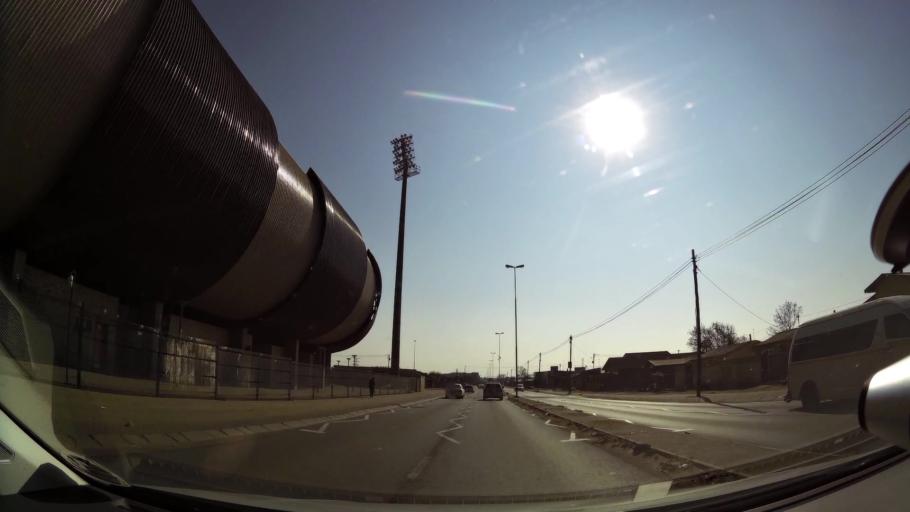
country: ZA
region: Orange Free State
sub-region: Mangaung Metropolitan Municipality
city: Bloemfontein
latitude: -29.1742
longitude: 26.2344
